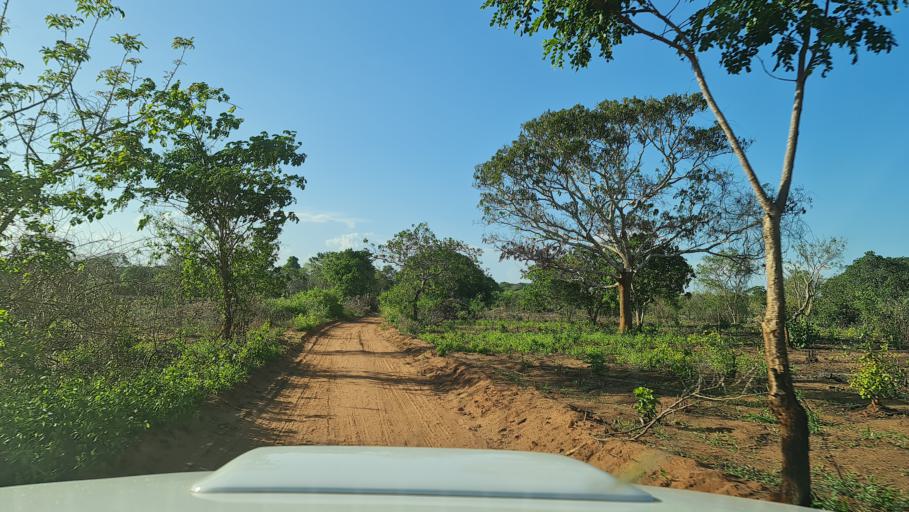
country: MZ
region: Nampula
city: Nacala
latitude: -14.7032
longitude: 40.3305
